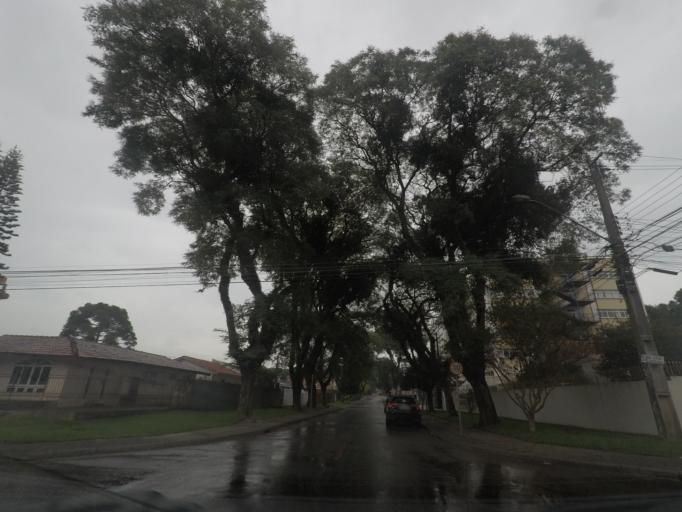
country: BR
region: Parana
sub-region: Curitiba
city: Curitiba
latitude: -25.4769
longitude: -49.3014
